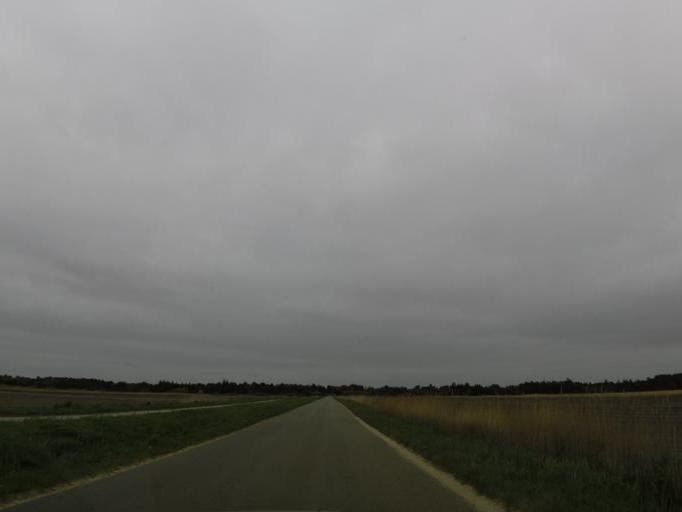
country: DE
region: Schleswig-Holstein
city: List
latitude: 55.0828
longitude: 8.5236
